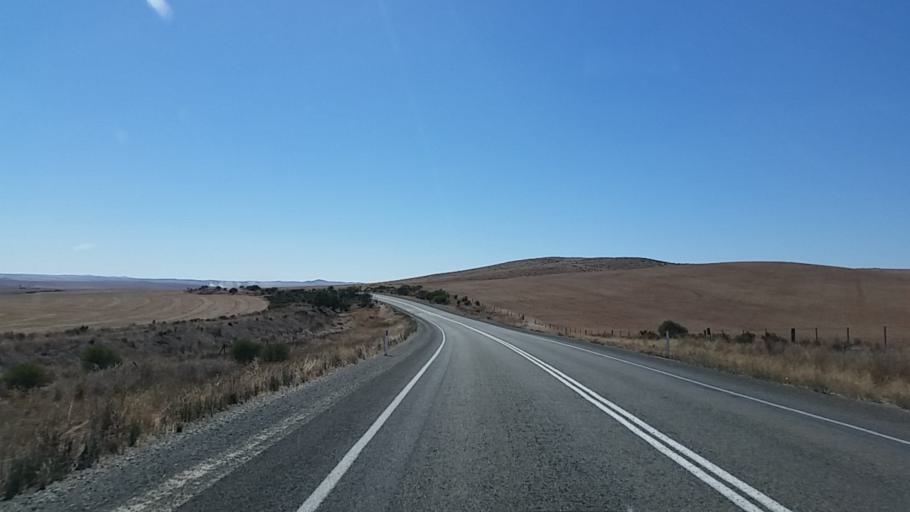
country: AU
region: South Australia
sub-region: Northern Areas
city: Jamestown
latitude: -33.3296
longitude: 138.8890
